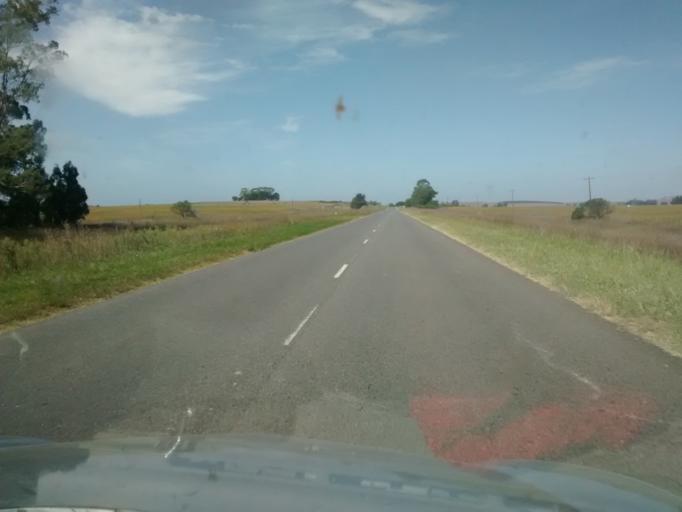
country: AR
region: Buenos Aires
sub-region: Partido de Balcarce
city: Balcarce
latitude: -37.6544
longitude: -58.4749
